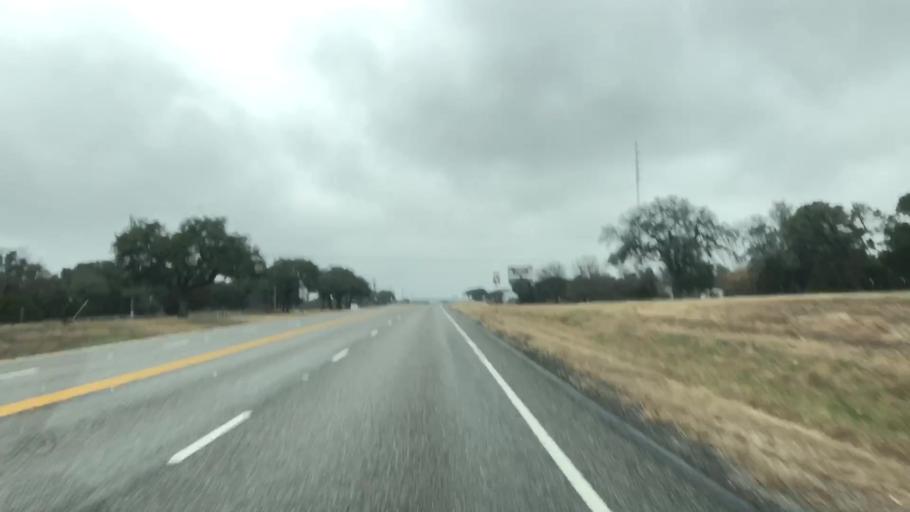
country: US
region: Texas
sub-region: Burnet County
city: Burnet
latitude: 30.8916
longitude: -98.2371
